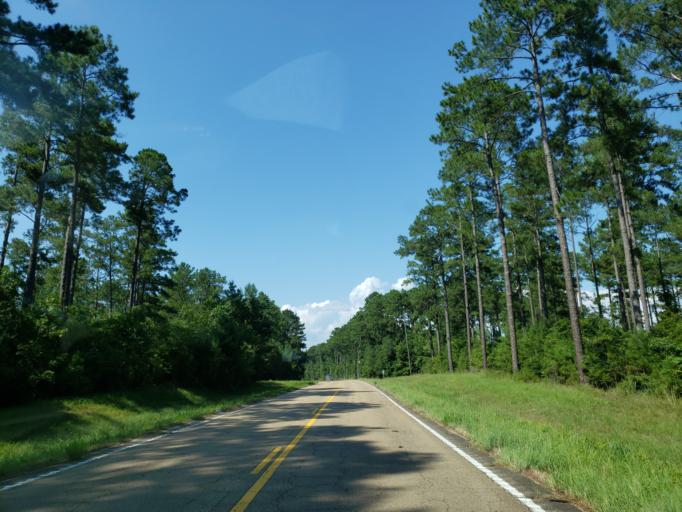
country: US
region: Mississippi
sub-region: Lamar County
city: Sumrall
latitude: 31.4431
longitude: -89.5302
